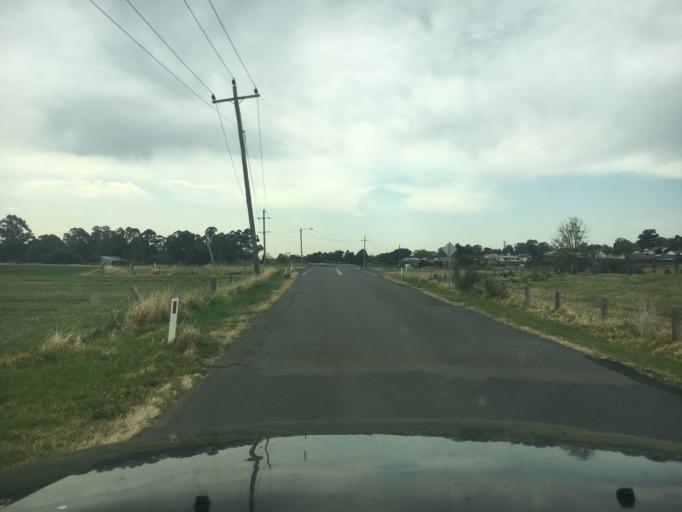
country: AU
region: New South Wales
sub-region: Maitland Municipality
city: East Maitland
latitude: -32.7514
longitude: 151.5713
